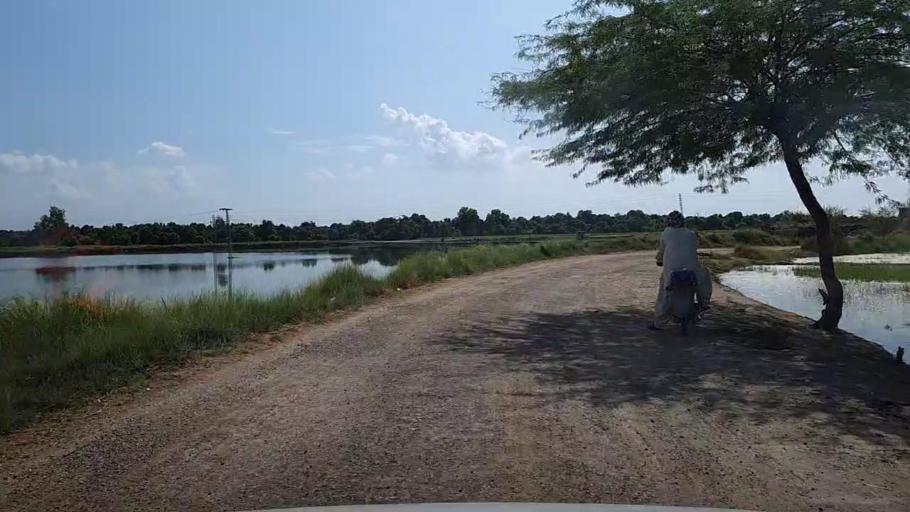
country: PK
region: Sindh
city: Bhiria
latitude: 26.9121
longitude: 68.2265
